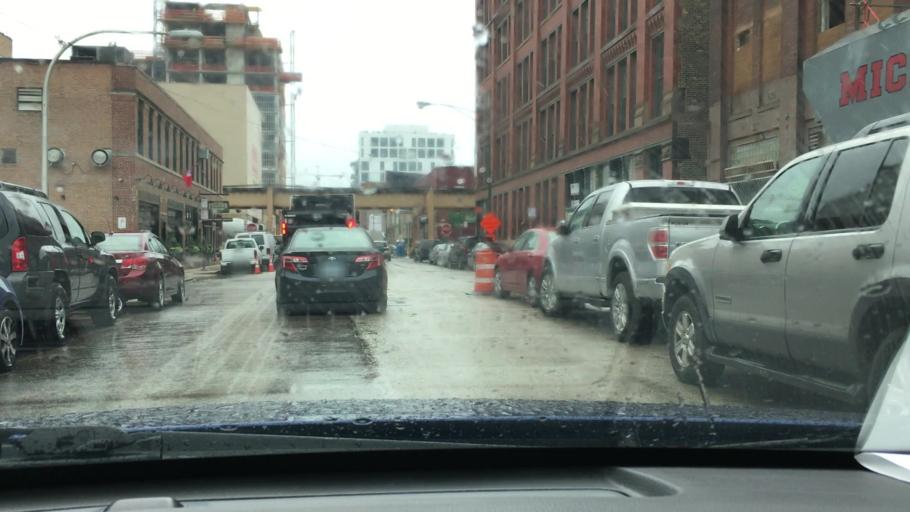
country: US
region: Illinois
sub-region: Cook County
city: Chicago
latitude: 41.8864
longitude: -87.6498
